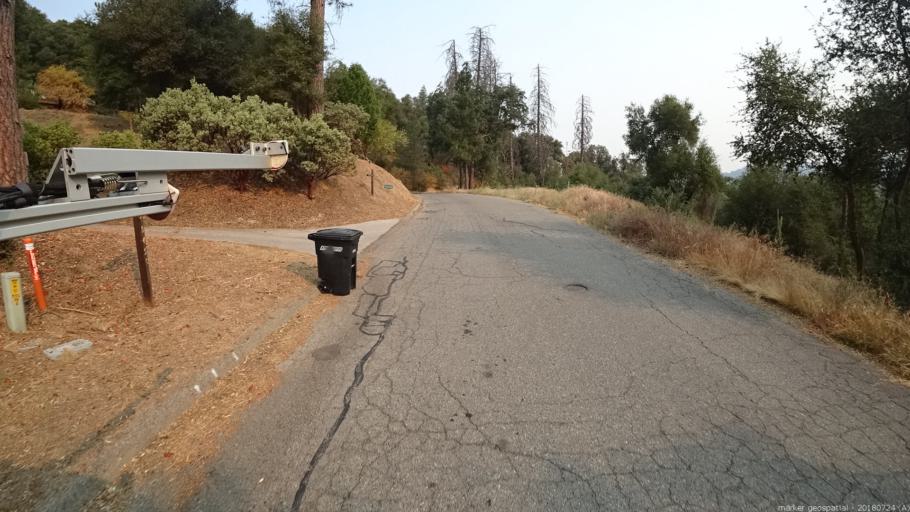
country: US
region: California
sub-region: Madera County
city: Oakhurst
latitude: 37.3194
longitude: -119.6275
